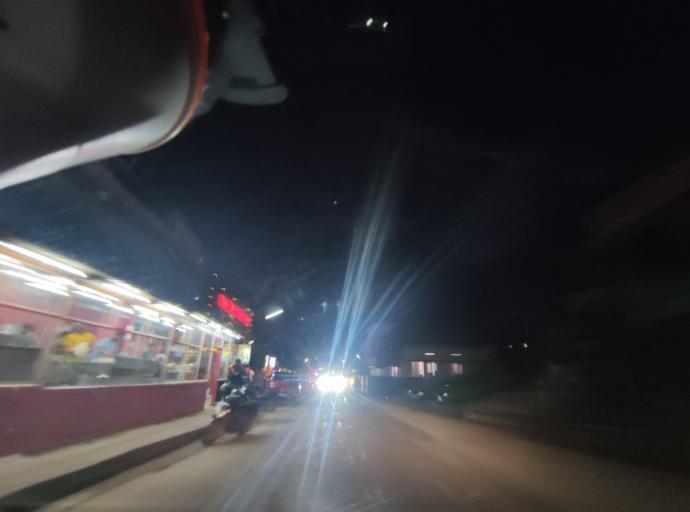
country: IN
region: Kerala
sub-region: Thiruvananthapuram
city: Nedumangad
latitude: 8.5624
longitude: 76.9561
